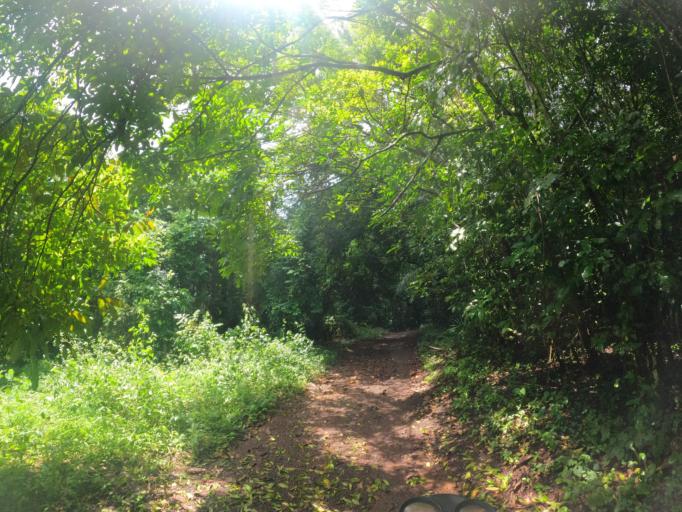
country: SL
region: Northern Province
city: Binkolo
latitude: 9.1601
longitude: -12.1914
